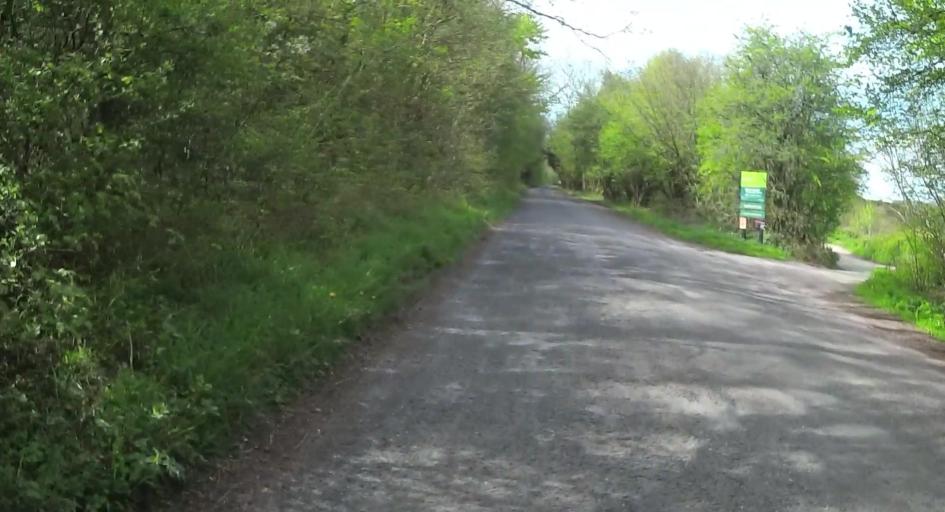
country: GB
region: England
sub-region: Hampshire
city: Chandlers Ford
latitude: 51.0608
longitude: -1.4005
